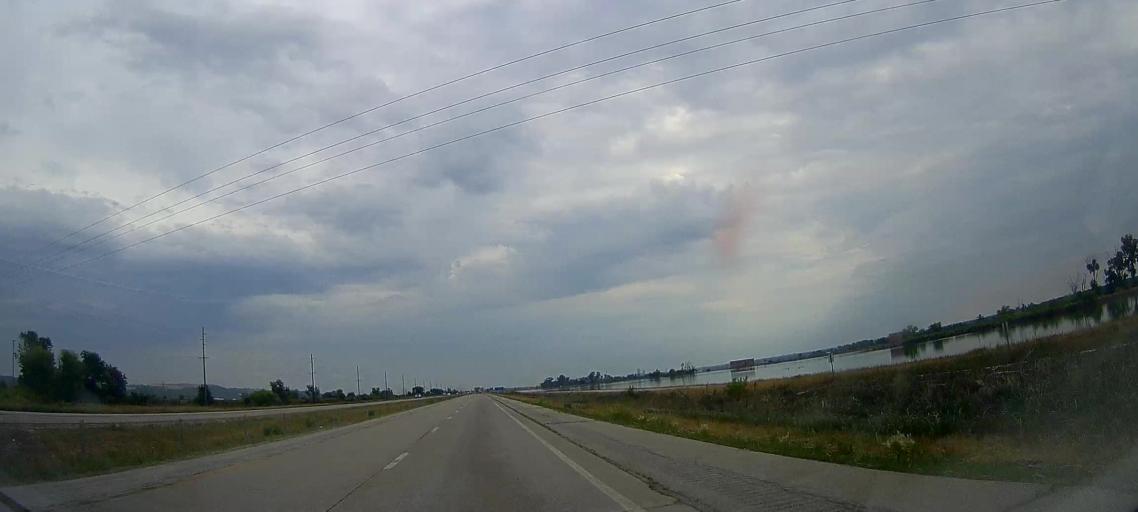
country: US
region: Iowa
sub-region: Pottawattamie County
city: Carter Lake
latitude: 41.3831
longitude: -95.8996
